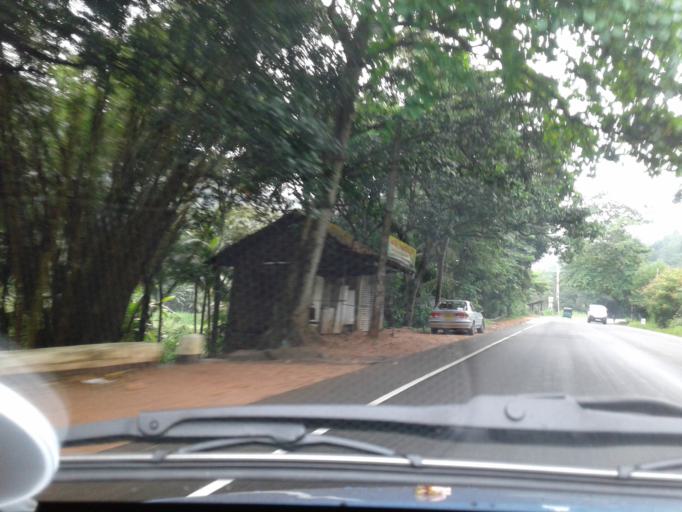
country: LK
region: Central
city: Kadugannawa
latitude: 7.2326
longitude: 80.2500
